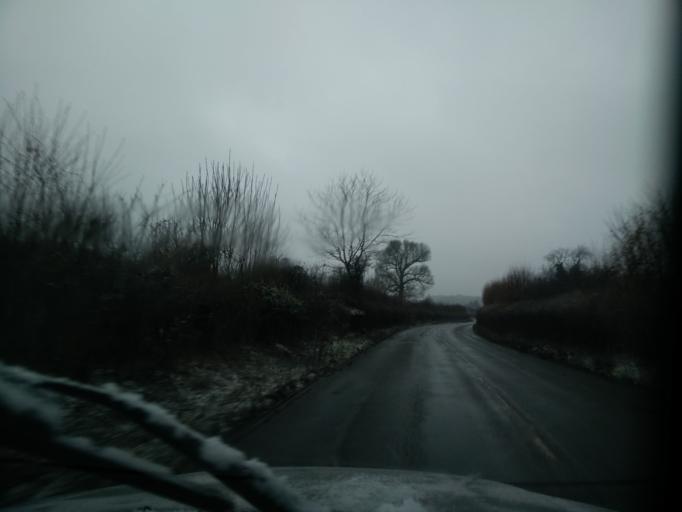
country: GB
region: England
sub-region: Buckinghamshire
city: Wendover
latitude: 51.7176
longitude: -0.7644
